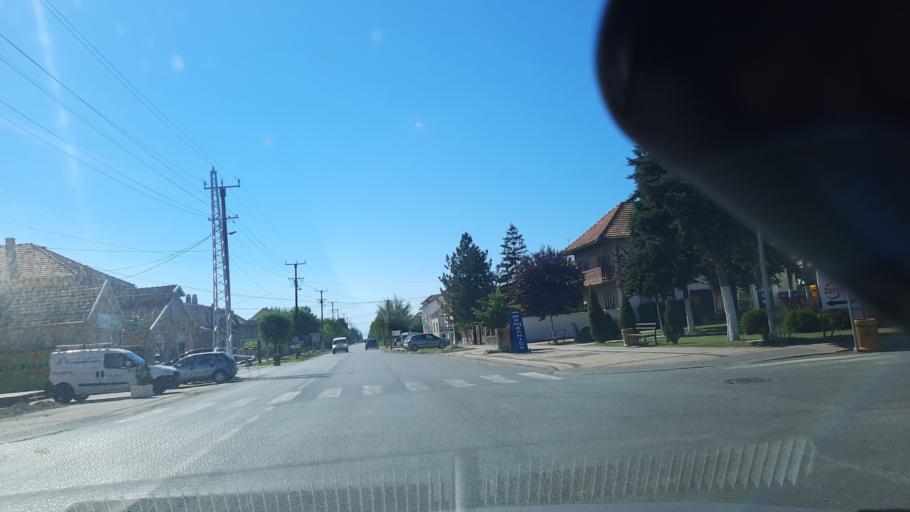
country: RS
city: Simanovci
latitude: 44.8745
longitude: 20.0892
